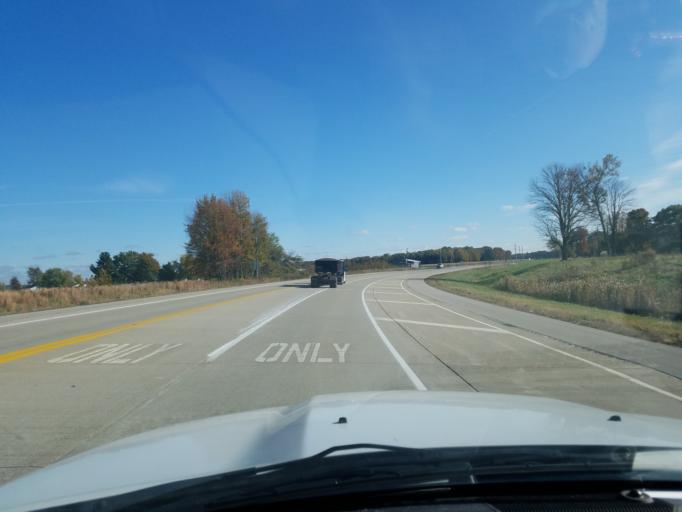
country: US
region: Indiana
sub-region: Jennings County
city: North Vernon
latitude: 39.0328
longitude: -85.6438
